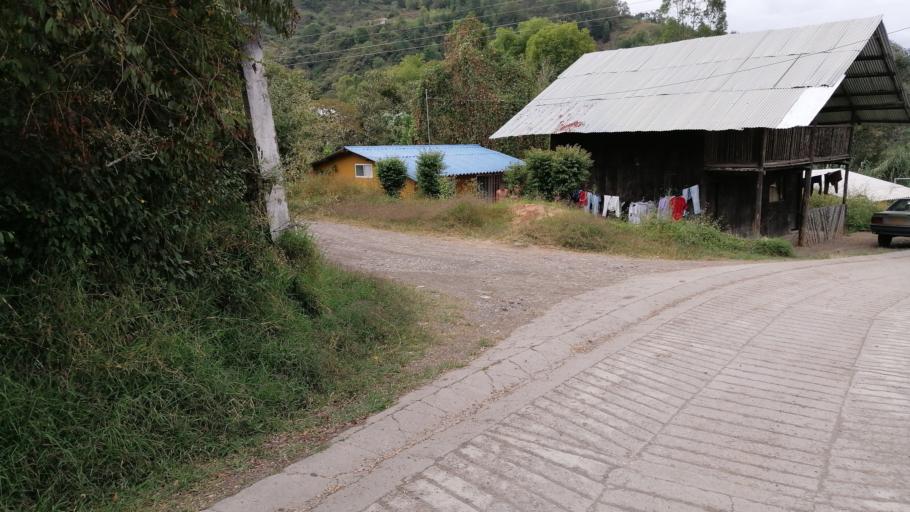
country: CO
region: Cundinamarca
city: Tenza
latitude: 5.0566
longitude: -73.4265
